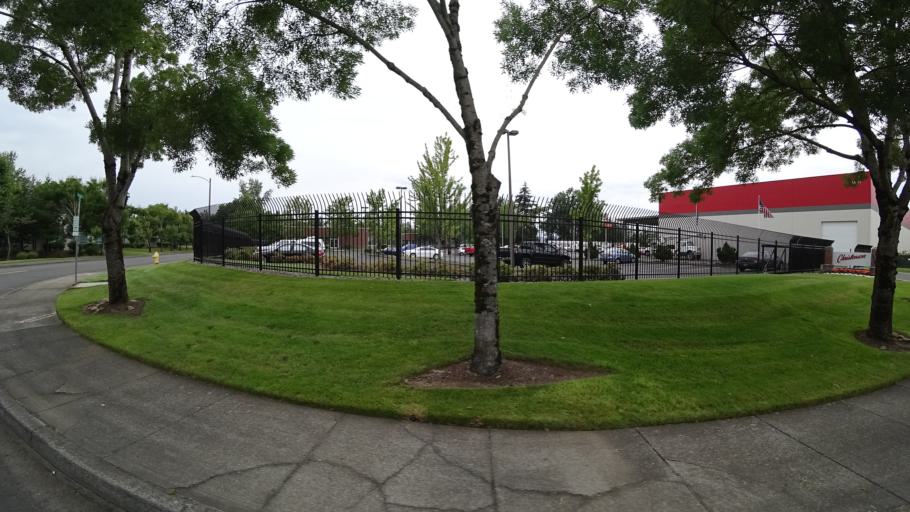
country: US
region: Oregon
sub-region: Multnomah County
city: Fairview
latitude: 45.5407
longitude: -122.4853
